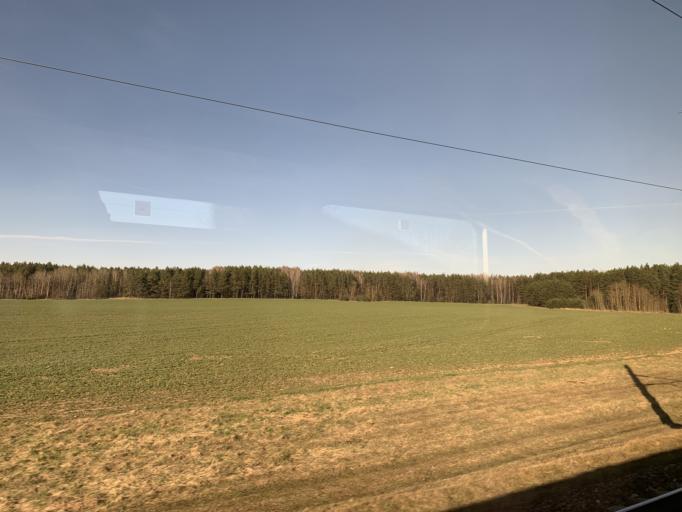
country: BY
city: Soly
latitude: 54.4940
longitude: 26.2795
